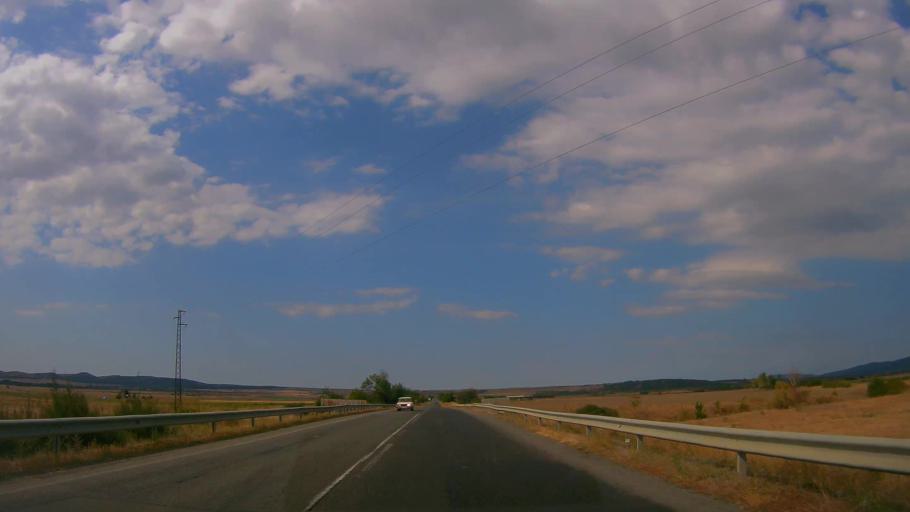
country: BG
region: Burgas
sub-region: Obshtina Aytos
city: Aytos
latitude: 42.7033
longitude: 27.2250
